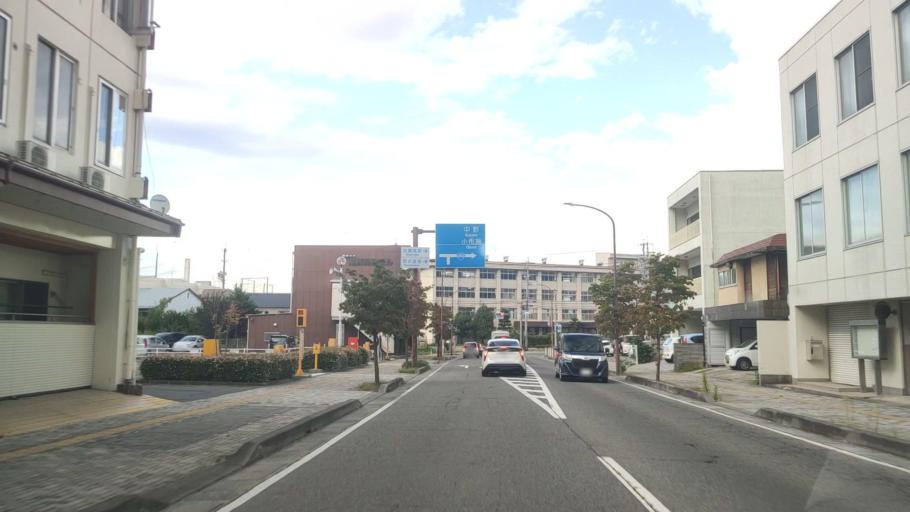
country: JP
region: Nagano
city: Suzaka
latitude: 36.6574
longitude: 138.3079
